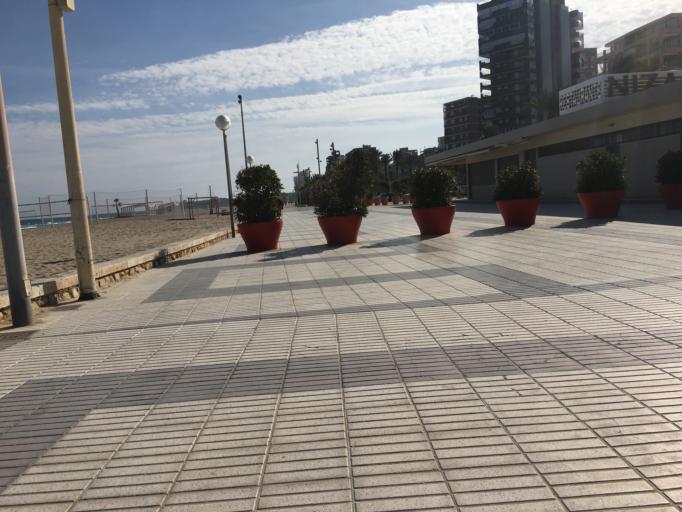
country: ES
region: Valencia
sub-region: Provincia de Alicante
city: San Juan de Alicante
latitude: 38.3762
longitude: -0.4101
